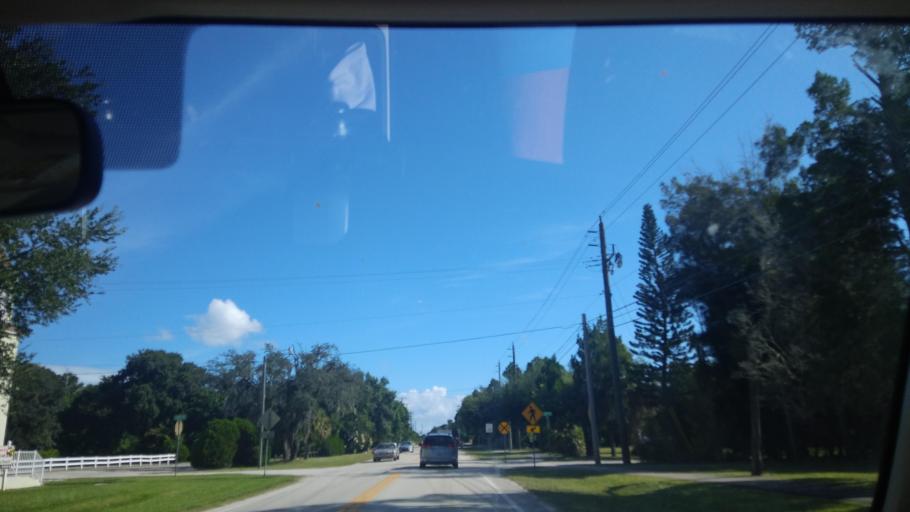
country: US
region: Florida
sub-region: Indian River County
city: Roseland
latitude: 27.8339
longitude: -80.4945
